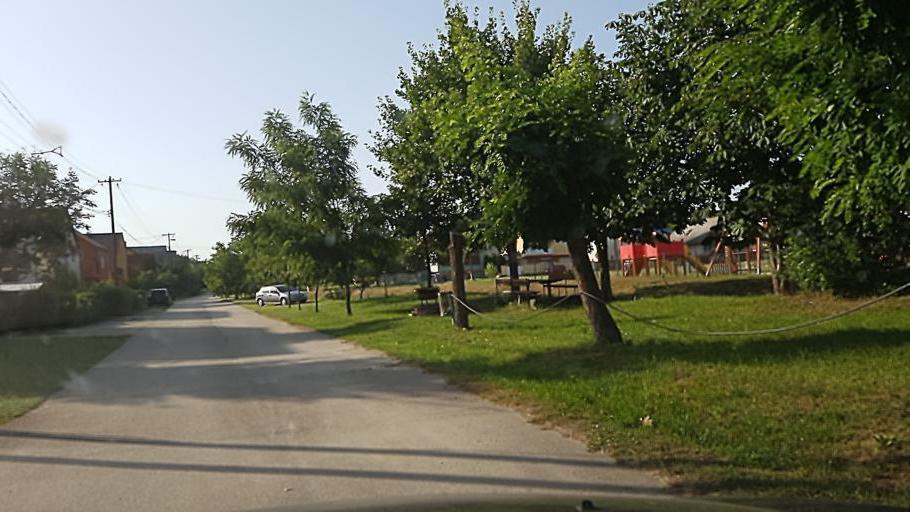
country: HU
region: Komarom-Esztergom
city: Kesztolc
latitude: 47.7109
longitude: 18.7820
